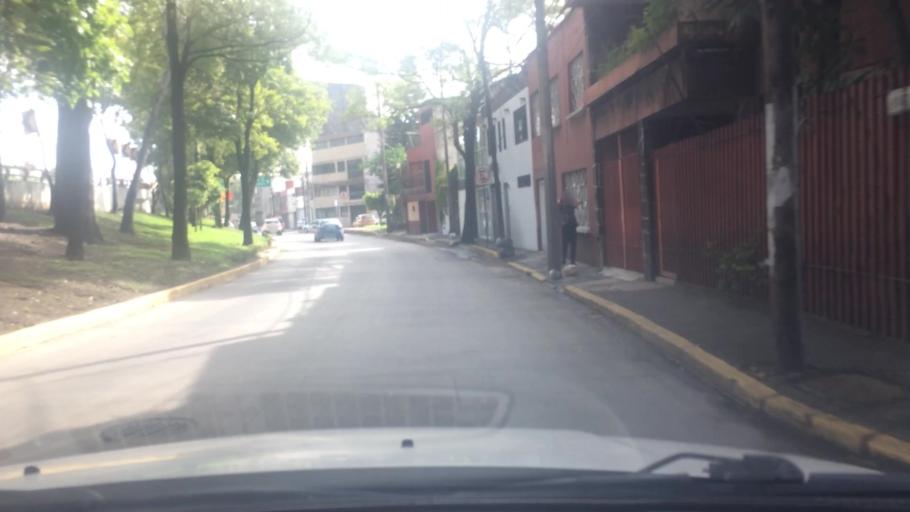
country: MX
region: Mexico City
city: Colonia Nativitas
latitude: 19.3571
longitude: -99.1320
